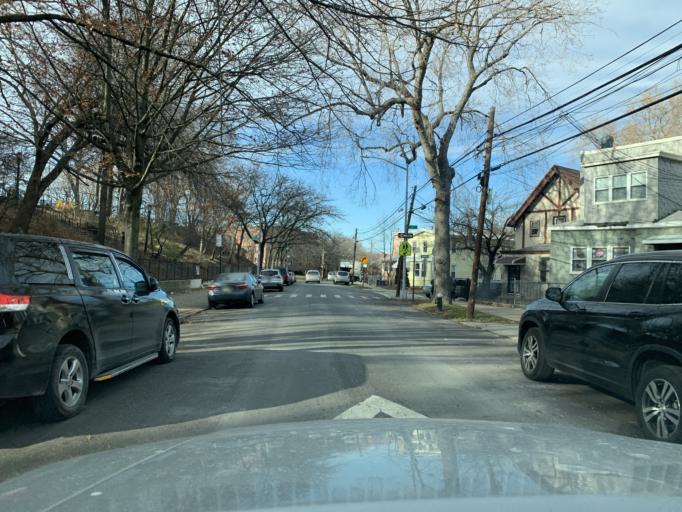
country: US
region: New York
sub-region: Queens County
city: Long Island City
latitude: 40.7471
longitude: -73.9092
